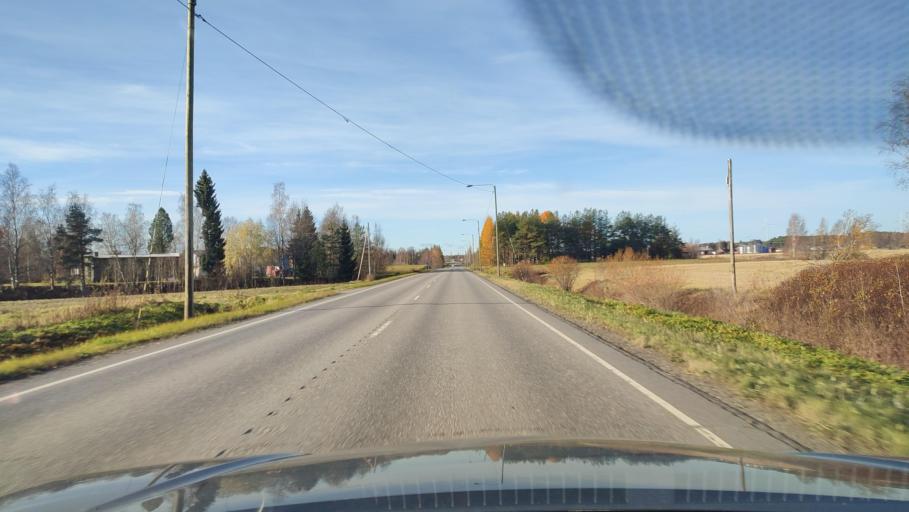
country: FI
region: Southern Ostrobothnia
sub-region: Suupohja
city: Teuva
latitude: 62.4918
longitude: 21.7639
